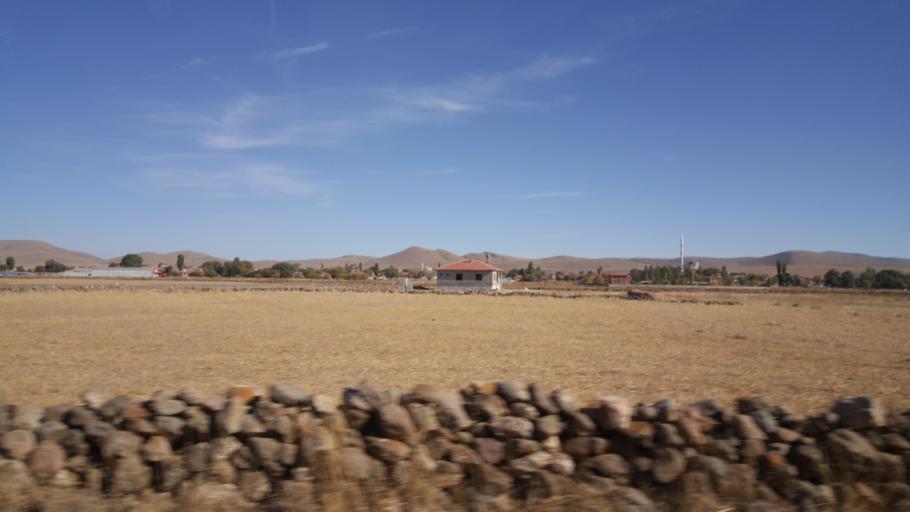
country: TR
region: Ankara
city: Altpinar
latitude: 39.2657
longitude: 32.7533
